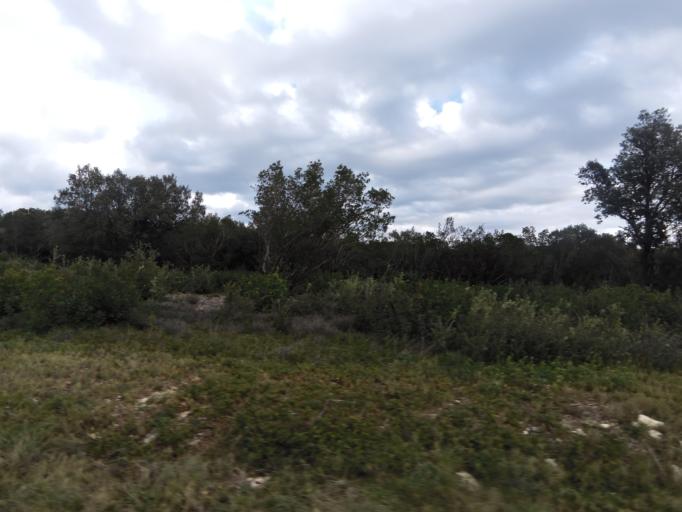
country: FR
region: Languedoc-Roussillon
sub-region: Departement du Gard
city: Clarensac
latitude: 43.8377
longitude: 4.1912
